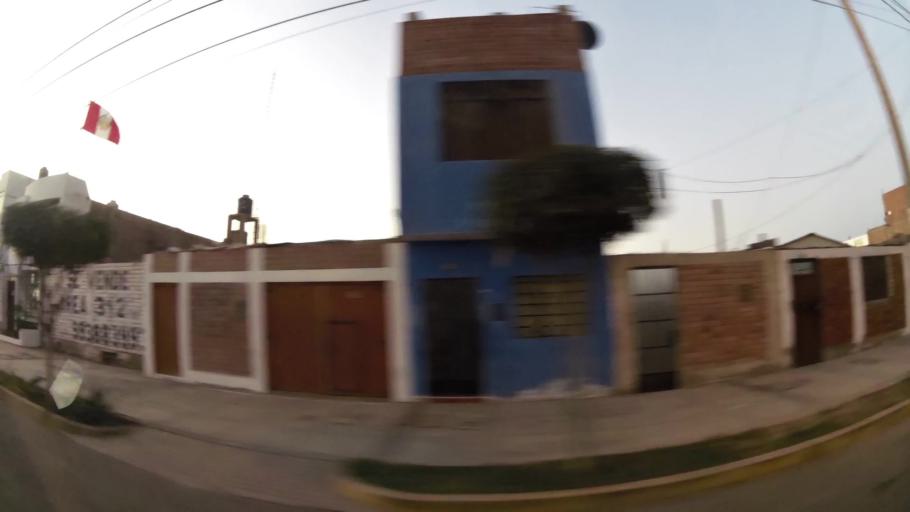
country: PE
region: Ica
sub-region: Provincia de Pisco
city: Pisco
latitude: -13.7095
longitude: -76.2145
